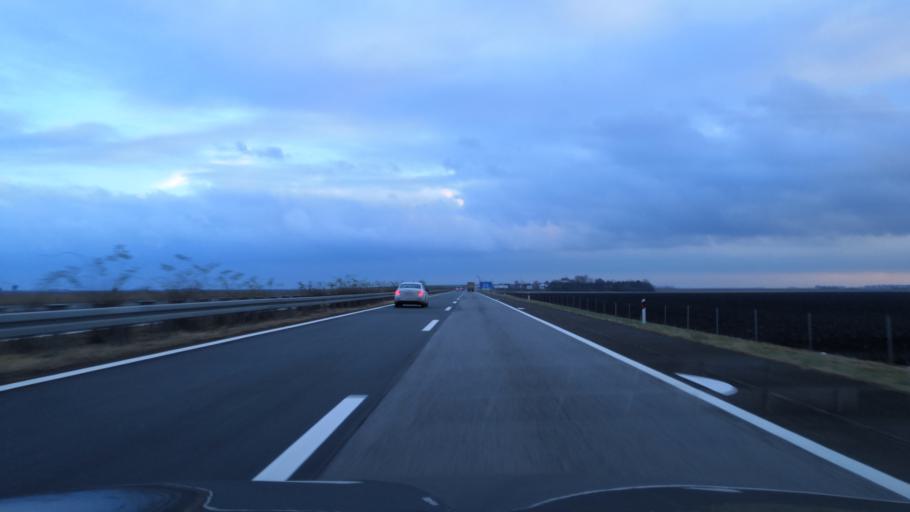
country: RS
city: Zmajevo
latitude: 45.5148
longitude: 19.7226
